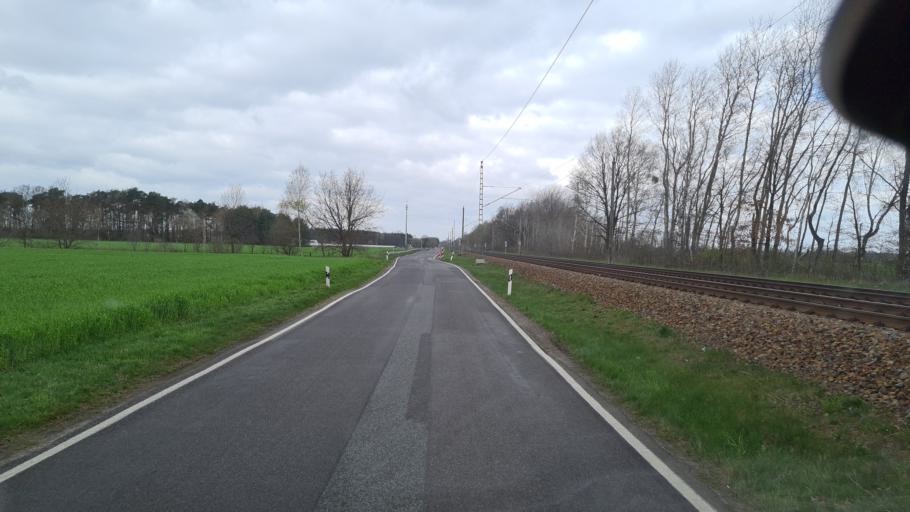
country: DE
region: Brandenburg
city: Ruhland
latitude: 51.4565
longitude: 13.8997
